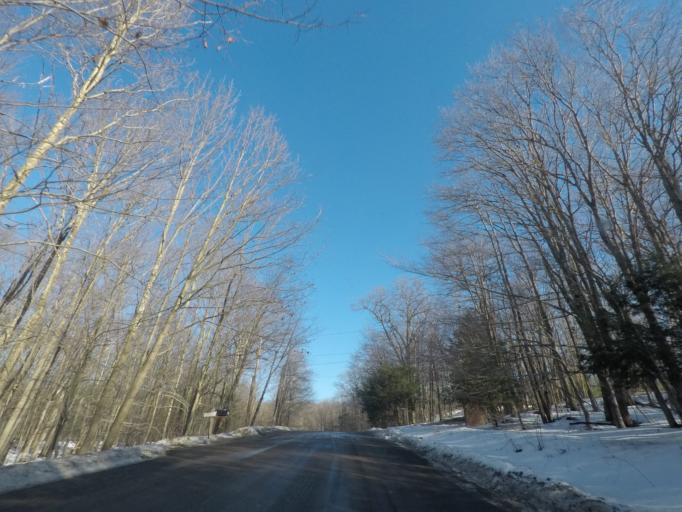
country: US
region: New York
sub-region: Rensselaer County
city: Averill Park
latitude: 42.6432
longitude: -73.5051
